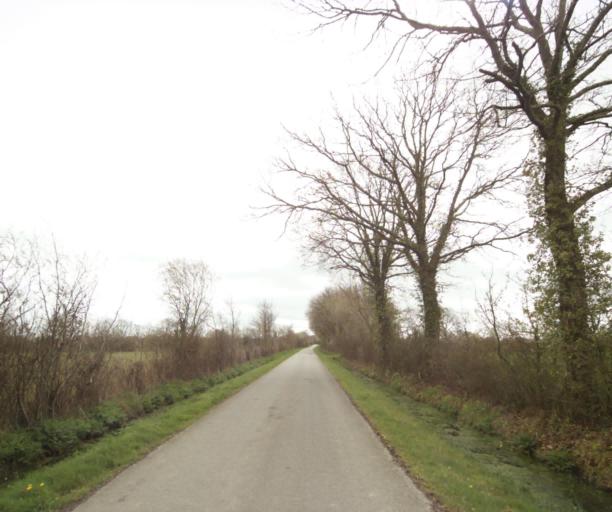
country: FR
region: Pays de la Loire
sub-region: Departement de la Loire-Atlantique
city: Bouvron
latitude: 47.4412
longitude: -1.8672
